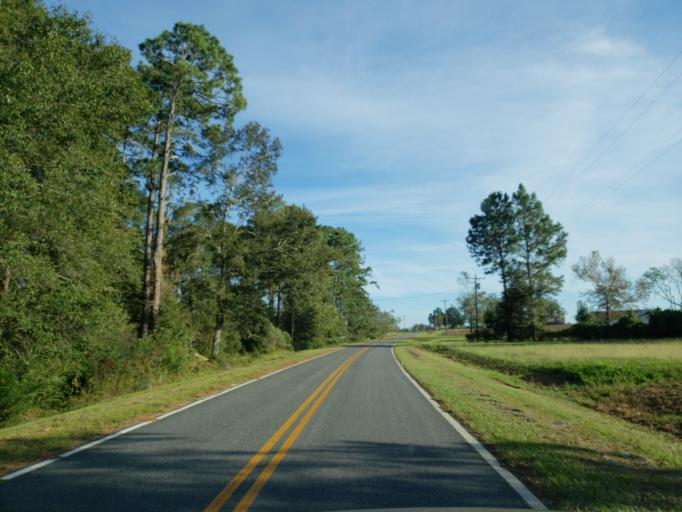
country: US
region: Georgia
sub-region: Dooly County
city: Vienna
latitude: 32.0454
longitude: -83.7560
